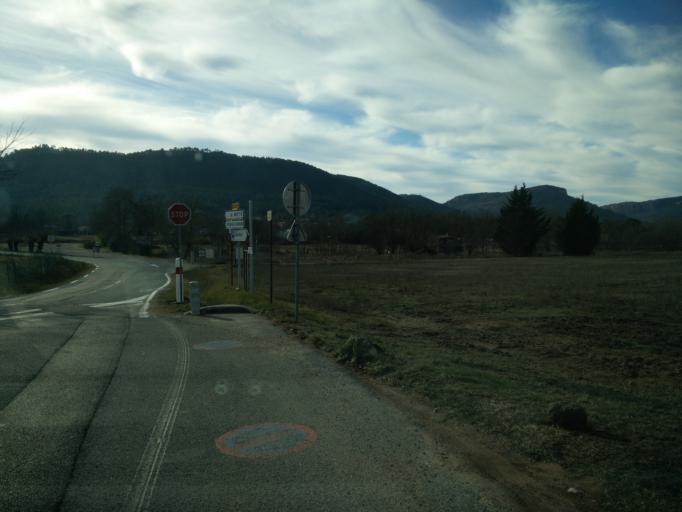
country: FR
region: Provence-Alpes-Cote d'Azur
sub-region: Departement du Var
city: Bagnols-en-Foret
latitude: 43.5377
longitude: 6.6893
